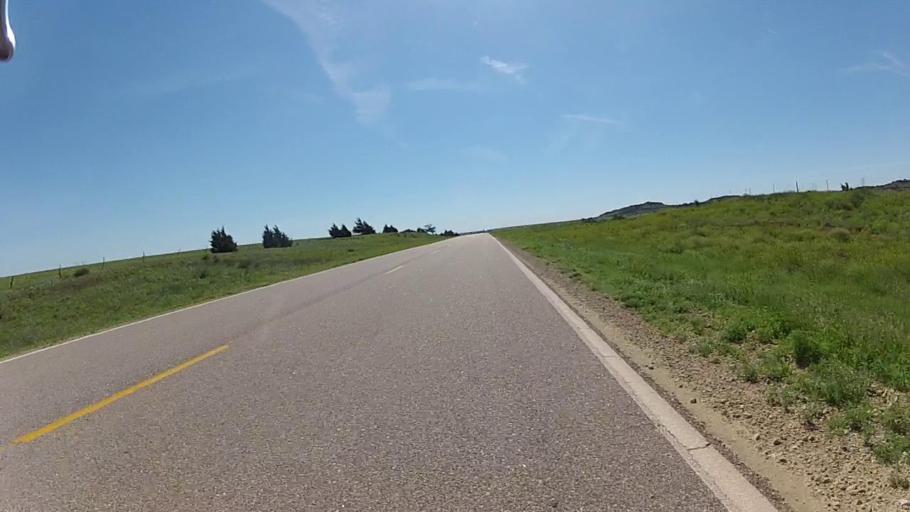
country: US
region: Kansas
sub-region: Barber County
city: Medicine Lodge
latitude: 37.2753
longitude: -98.7239
